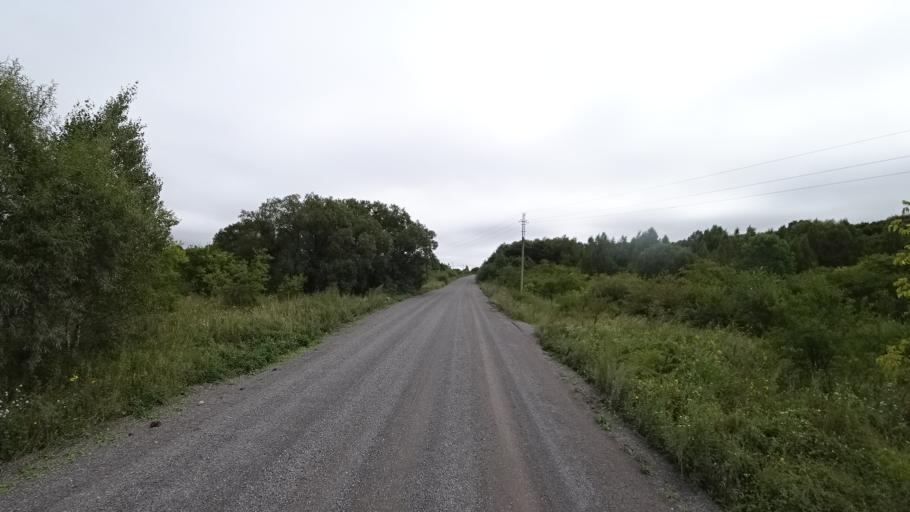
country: RU
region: Primorskiy
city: Lyalichi
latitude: 44.0733
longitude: 132.4759
